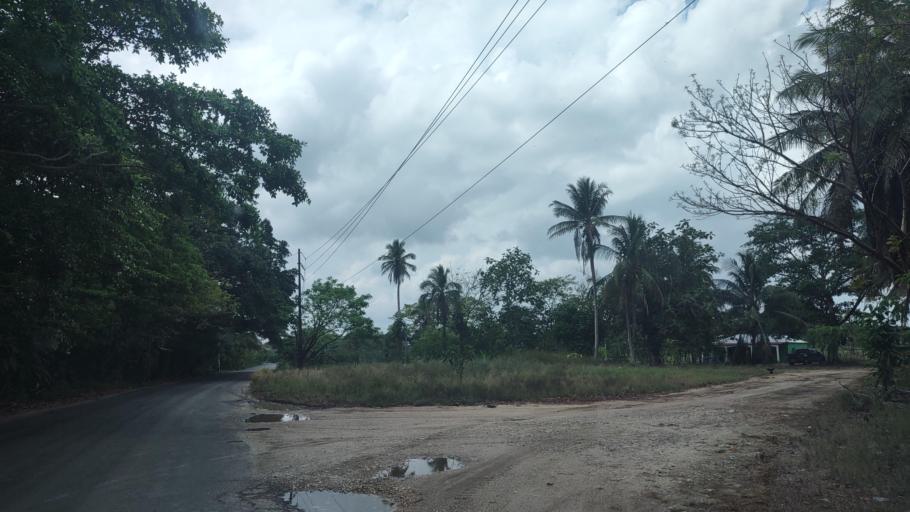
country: MX
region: Veracruz
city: Las Choapas
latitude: 17.9639
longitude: -94.1108
